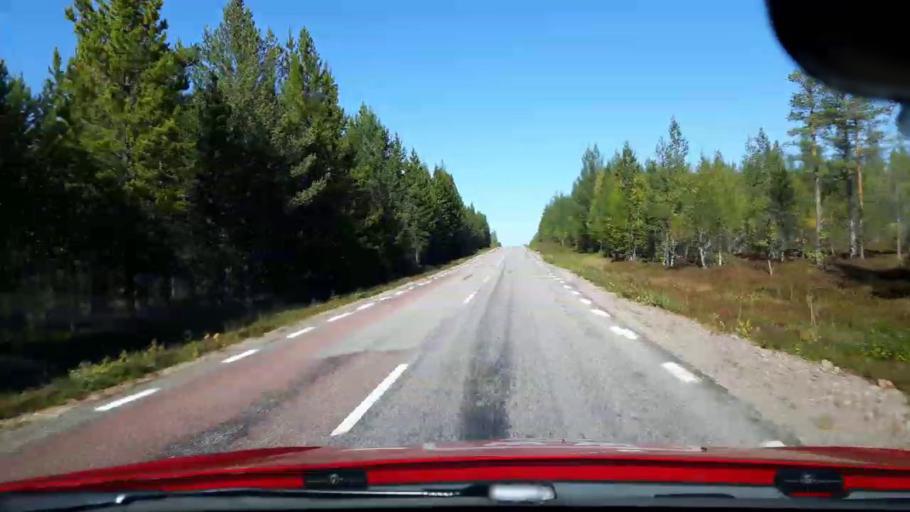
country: SE
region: Jaemtland
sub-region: Harjedalens Kommun
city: Sveg
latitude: 61.7262
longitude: 14.1663
